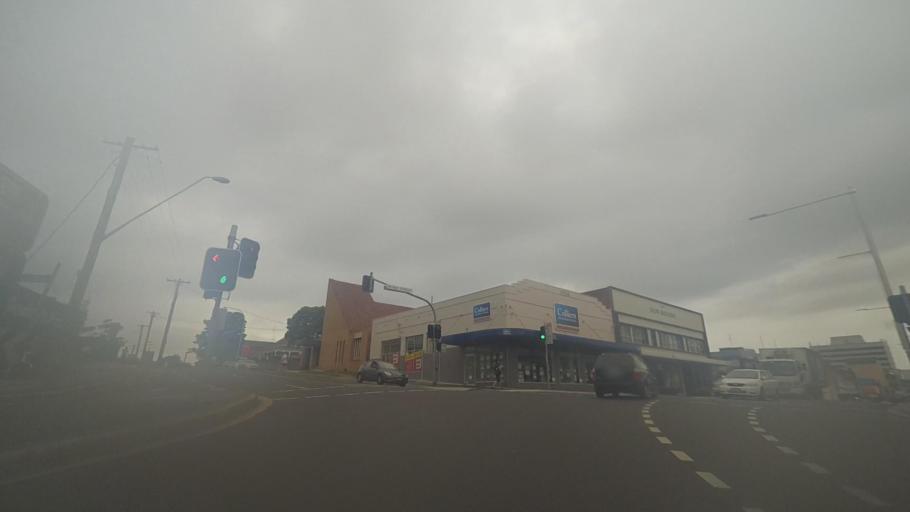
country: AU
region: New South Wales
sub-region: Wollongong
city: Wollongong
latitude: -34.4214
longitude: 150.8938
